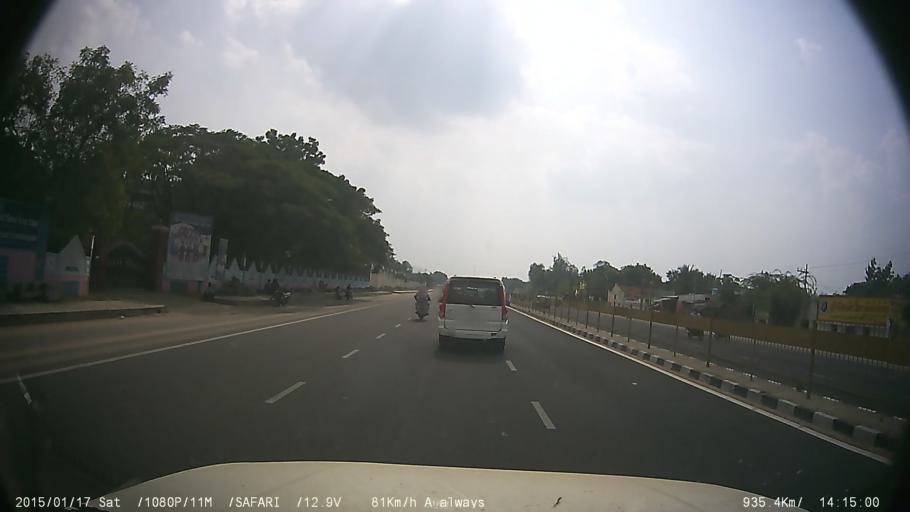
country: IN
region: Tamil Nadu
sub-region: Vellore
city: Ambur
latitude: 12.7702
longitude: 78.7099
